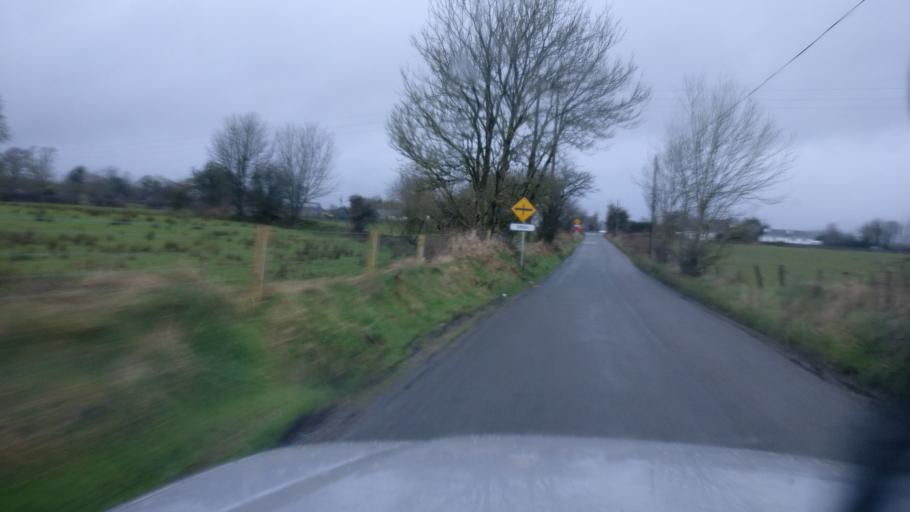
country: IE
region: Connaught
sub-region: County Galway
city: Loughrea
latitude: 53.2664
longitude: -8.4067
